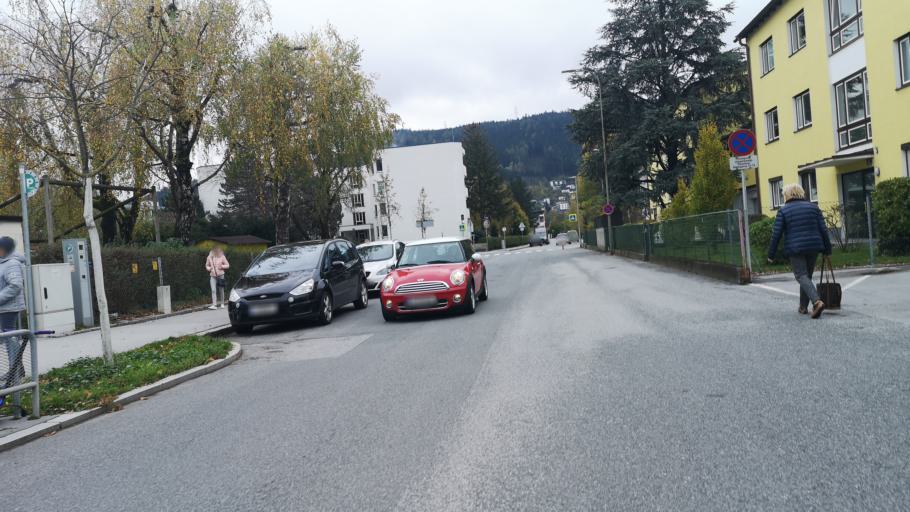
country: AT
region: Tyrol
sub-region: Innsbruck Stadt
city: Innsbruck
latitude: 47.2600
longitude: 11.3688
